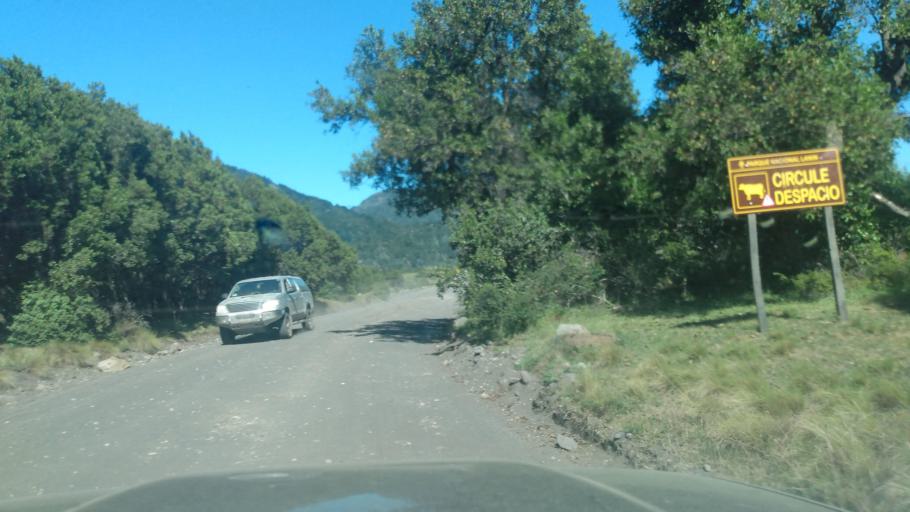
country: AR
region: Neuquen
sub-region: Departamento de Lacar
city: San Martin de los Andes
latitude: -39.7460
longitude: -71.5064
